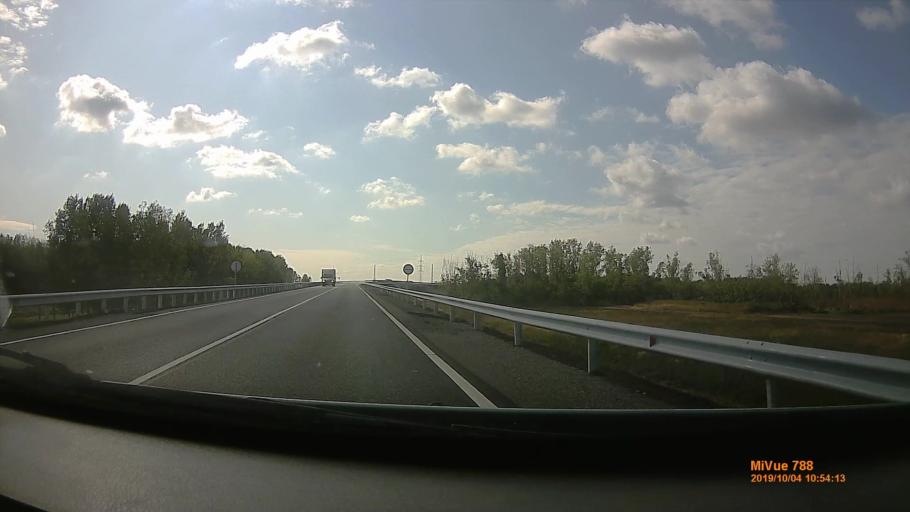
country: HU
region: Szabolcs-Szatmar-Bereg
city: Nyirtelek
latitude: 47.9825
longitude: 21.6653
